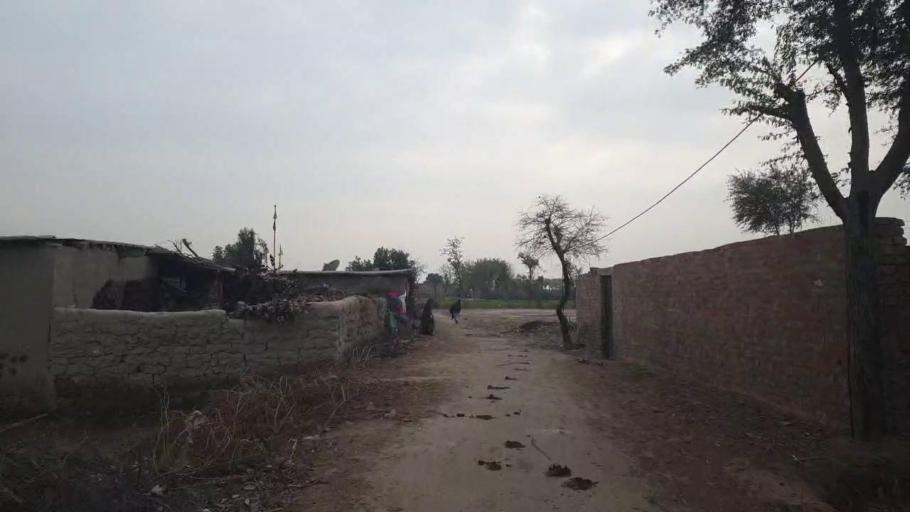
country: PK
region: Sindh
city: Tando Adam
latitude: 25.7745
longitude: 68.6455
